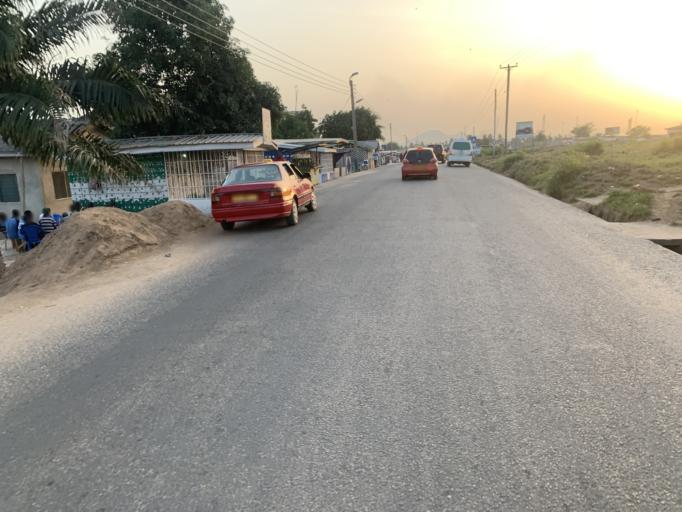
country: GH
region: Central
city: Winneba
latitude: 5.3522
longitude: -0.6190
